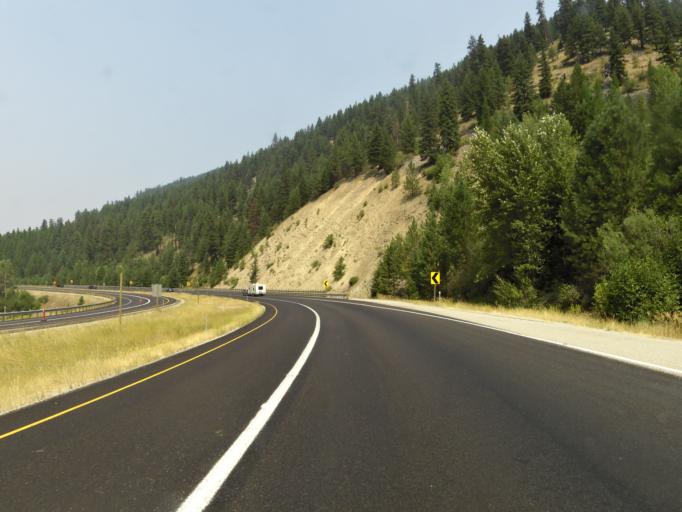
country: US
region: Montana
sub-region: Sanders County
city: Thompson Falls
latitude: 47.3258
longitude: -115.2499
